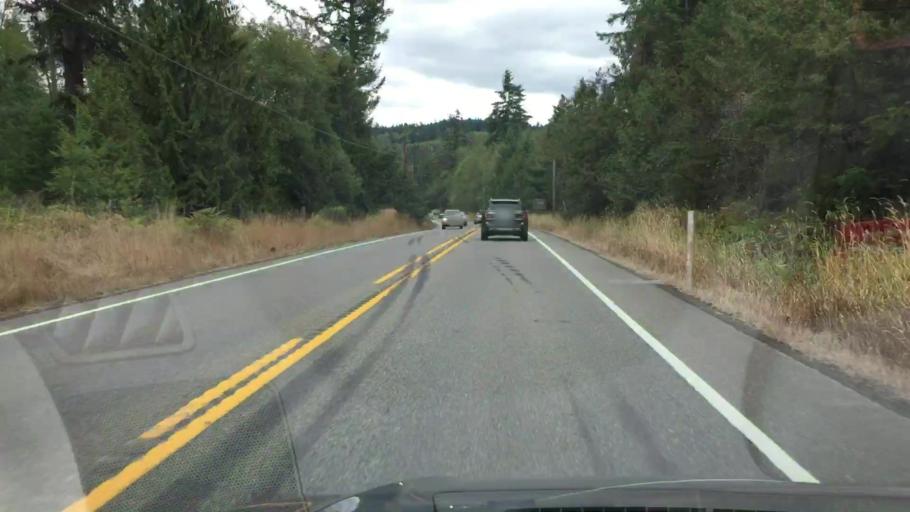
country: US
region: Washington
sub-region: Pierce County
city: Eatonville
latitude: 46.9458
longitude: -122.2881
